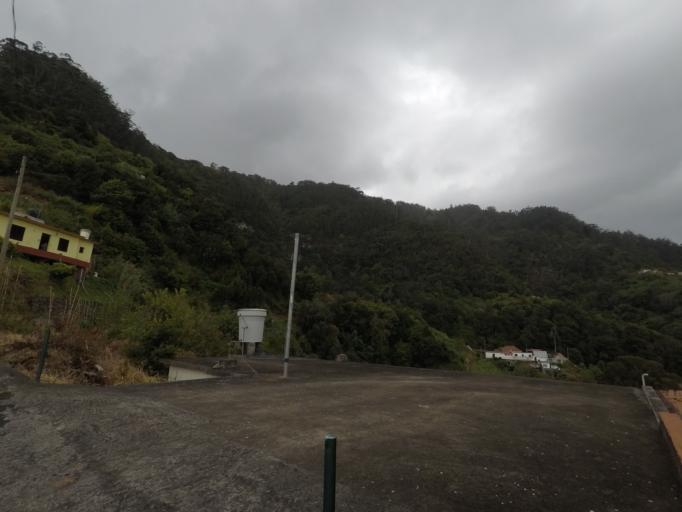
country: PT
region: Madeira
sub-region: Santana
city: Santana
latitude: 32.7527
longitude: -16.8264
